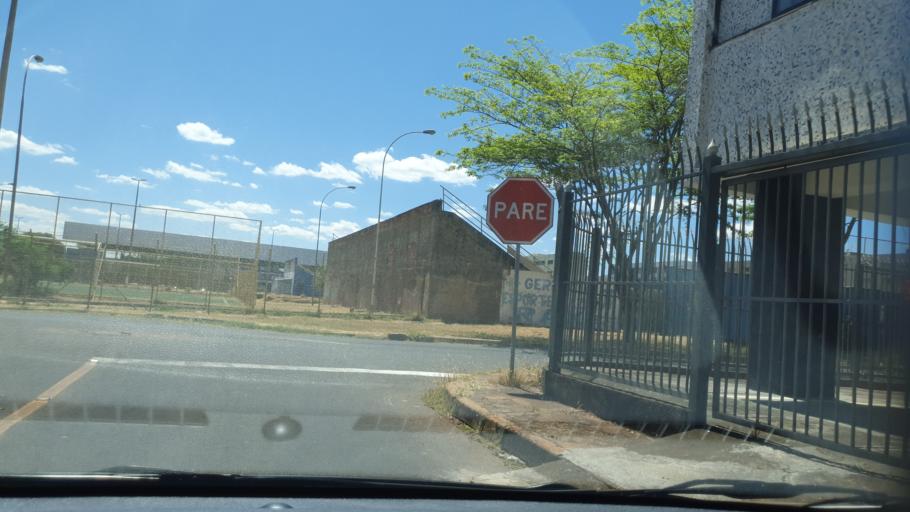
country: BR
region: Federal District
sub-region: Brasilia
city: Brasilia
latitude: -15.7934
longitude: -47.9387
